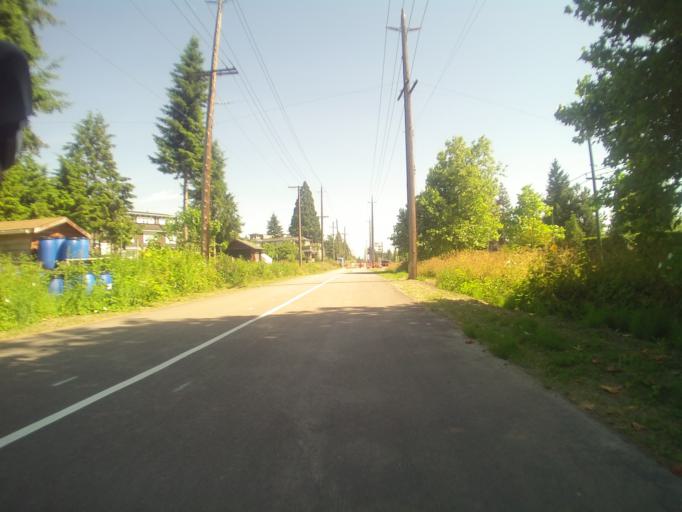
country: CA
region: British Columbia
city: Vancouver
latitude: 49.2205
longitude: -123.1510
